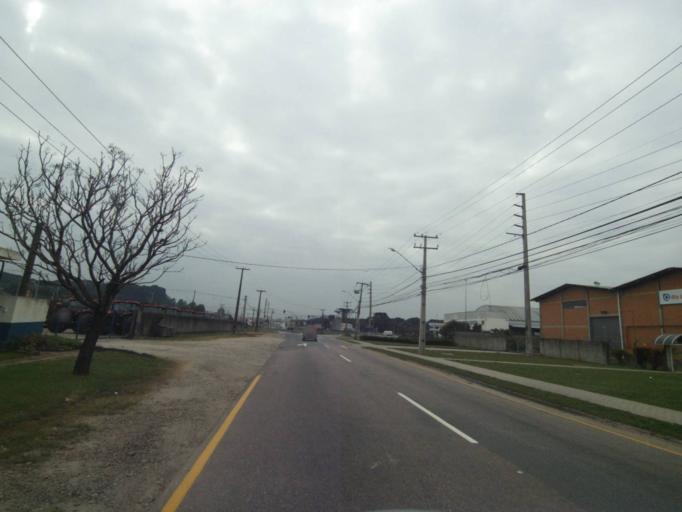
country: BR
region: Parana
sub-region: Curitiba
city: Curitiba
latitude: -25.5193
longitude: -49.3249
